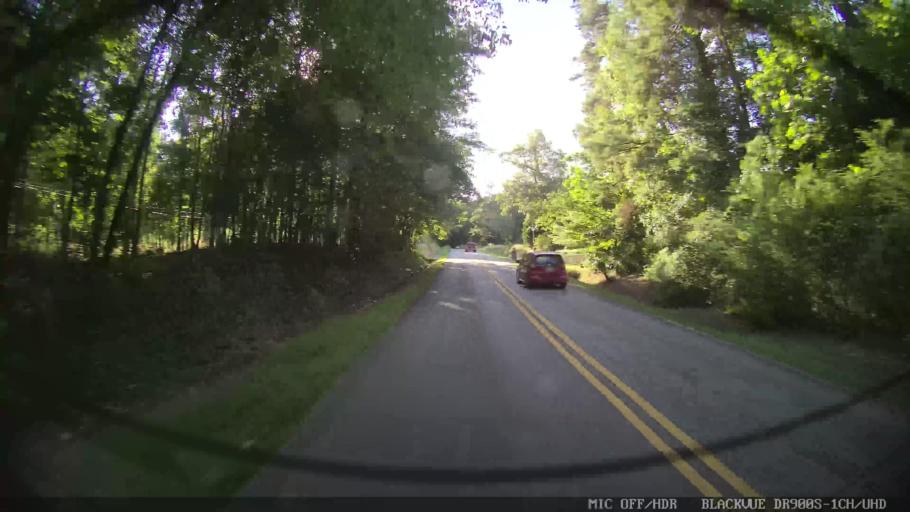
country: US
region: Georgia
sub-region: Floyd County
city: Rome
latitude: 34.2330
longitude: -85.1512
